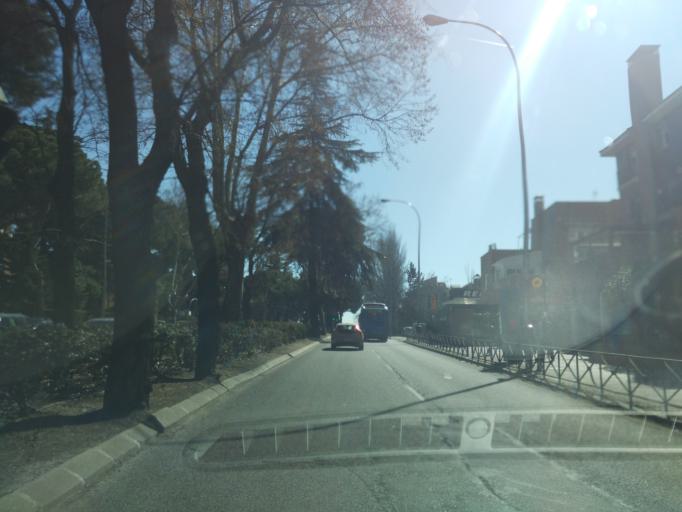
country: ES
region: Madrid
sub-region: Provincia de Madrid
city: Ciudad Lineal
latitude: 40.4580
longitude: -3.6586
